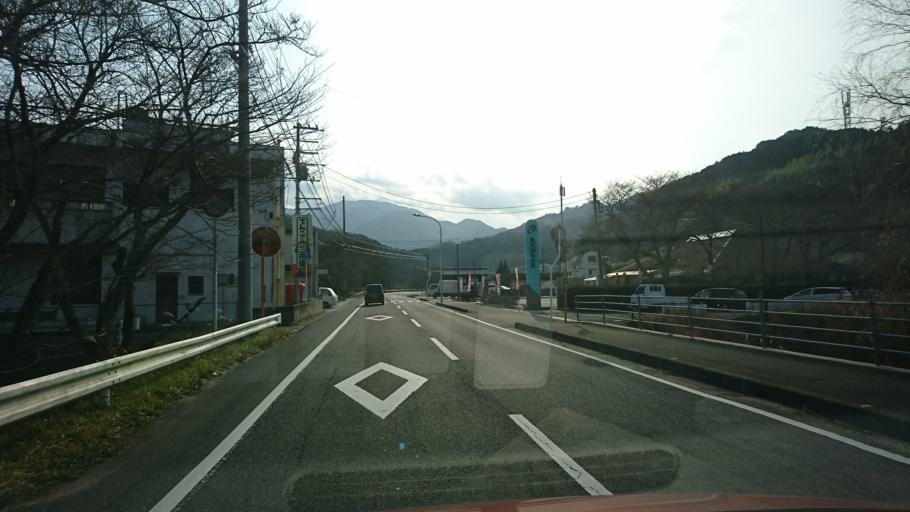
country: JP
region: Ehime
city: Hojo
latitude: 33.9931
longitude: 132.9149
